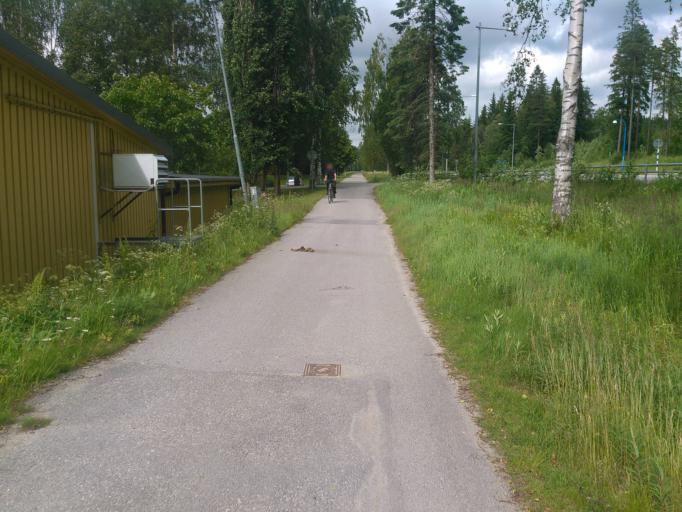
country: SE
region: Vaesterbotten
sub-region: Umea Kommun
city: Roback
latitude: 63.8641
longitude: 20.1990
